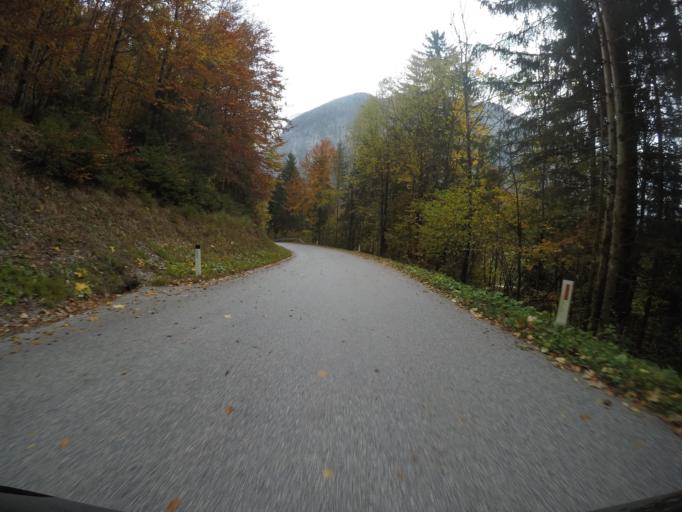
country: SI
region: Kranjska Gora
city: Mojstrana
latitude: 46.4326
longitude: 13.9335
